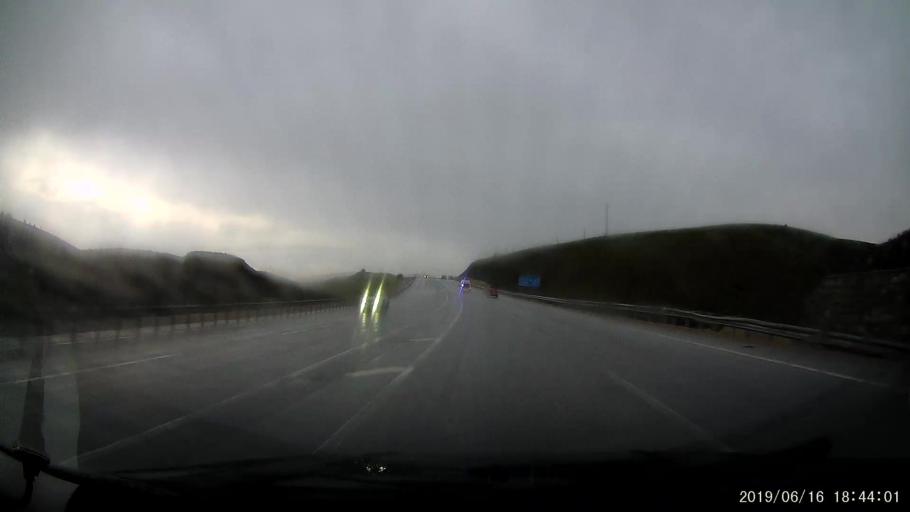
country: TR
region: Erzincan
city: Doganbeyli
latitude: 39.8710
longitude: 39.0809
